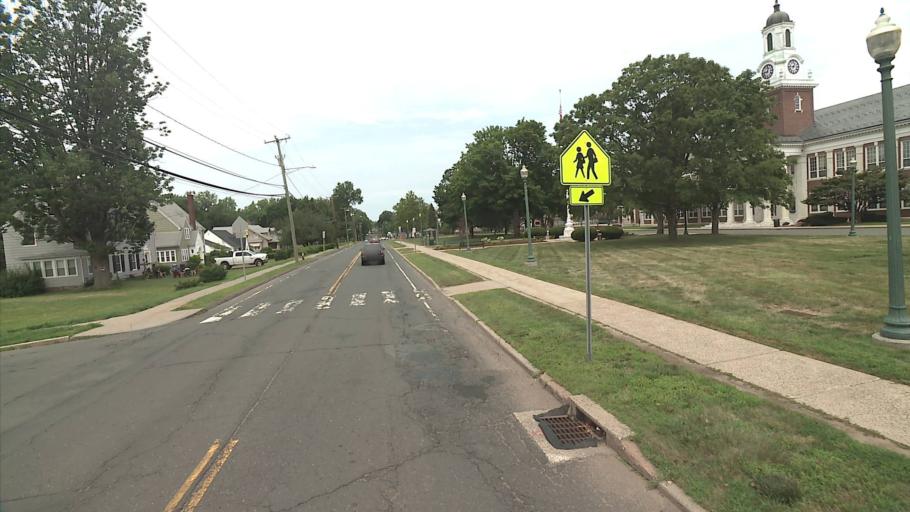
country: US
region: Connecticut
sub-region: Hartford County
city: New Britain
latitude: 41.6897
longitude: -72.7707
